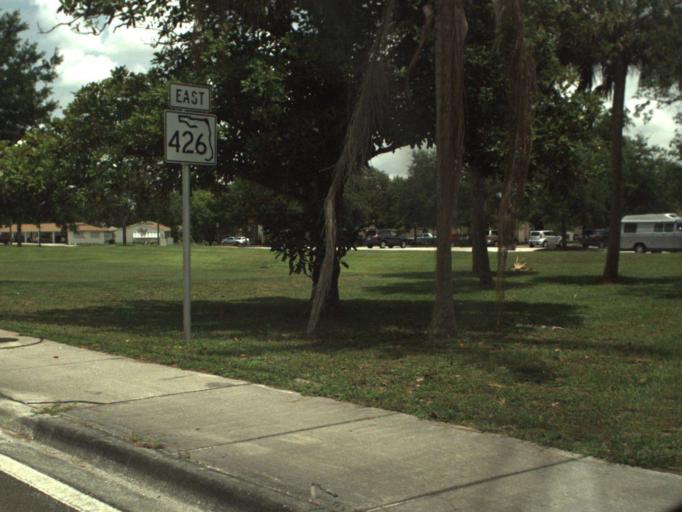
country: US
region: Florida
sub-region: Seminole County
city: Oviedo
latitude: 28.6420
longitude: -81.2332
